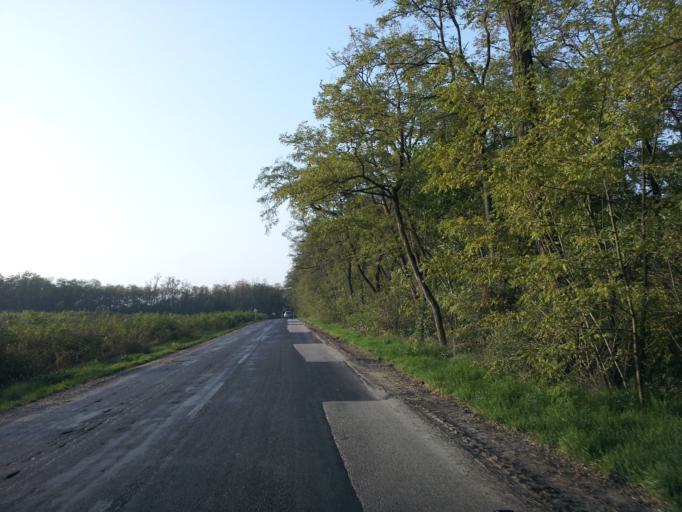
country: HU
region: Komarom-Esztergom
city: Kisber
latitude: 47.4859
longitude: 18.0582
